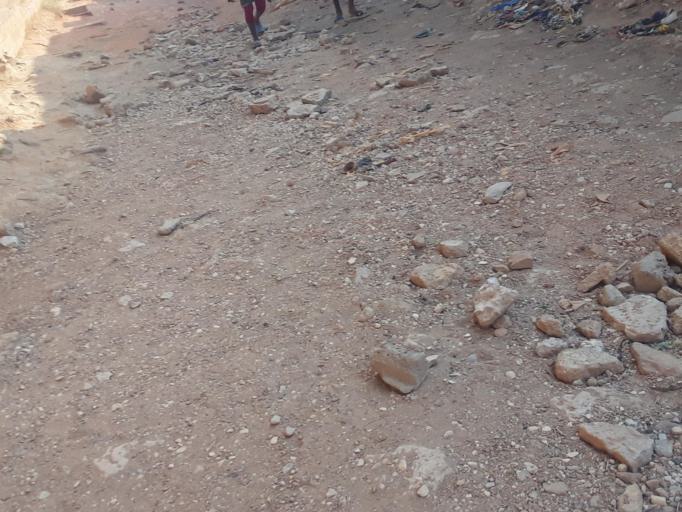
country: ZM
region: Lusaka
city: Lusaka
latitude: -15.3597
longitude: 28.2953
